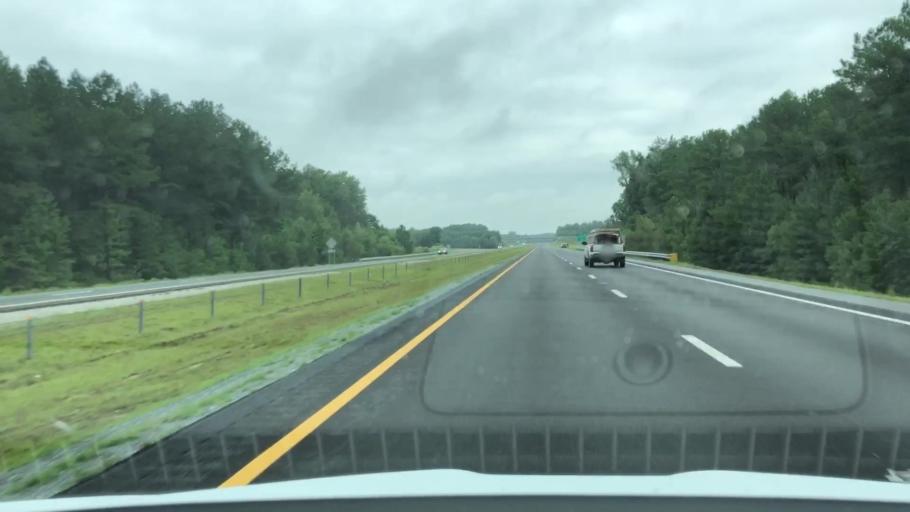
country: US
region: North Carolina
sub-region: Wayne County
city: Fremont
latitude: 35.4882
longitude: -77.9928
